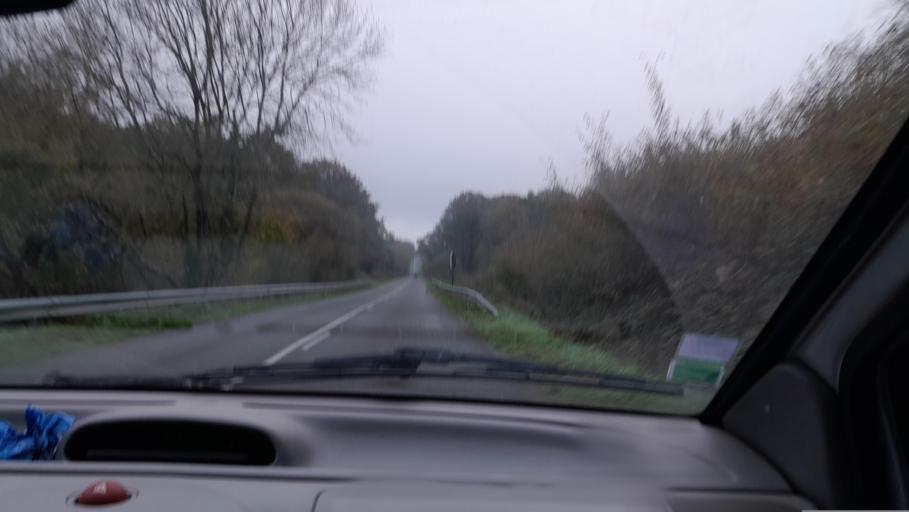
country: FR
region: Pays de la Loire
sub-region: Departement de la Mayenne
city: Ahuille
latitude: 48.0496
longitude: -0.8687
